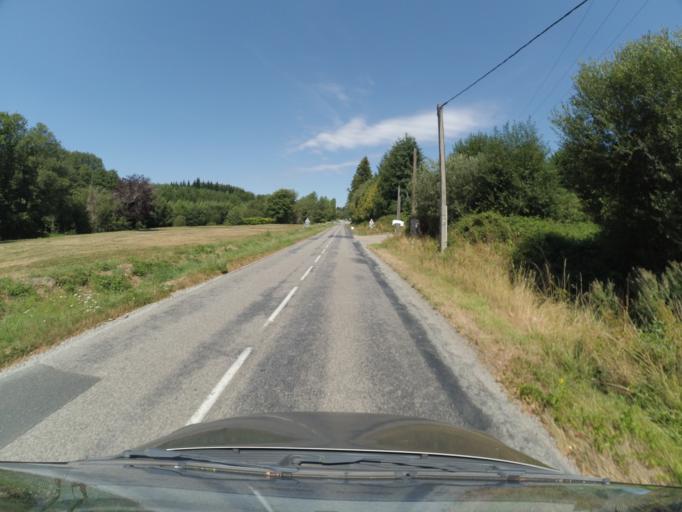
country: FR
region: Limousin
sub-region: Departement de la Creuse
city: Bourganeuf
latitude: 45.9657
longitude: 1.7580
